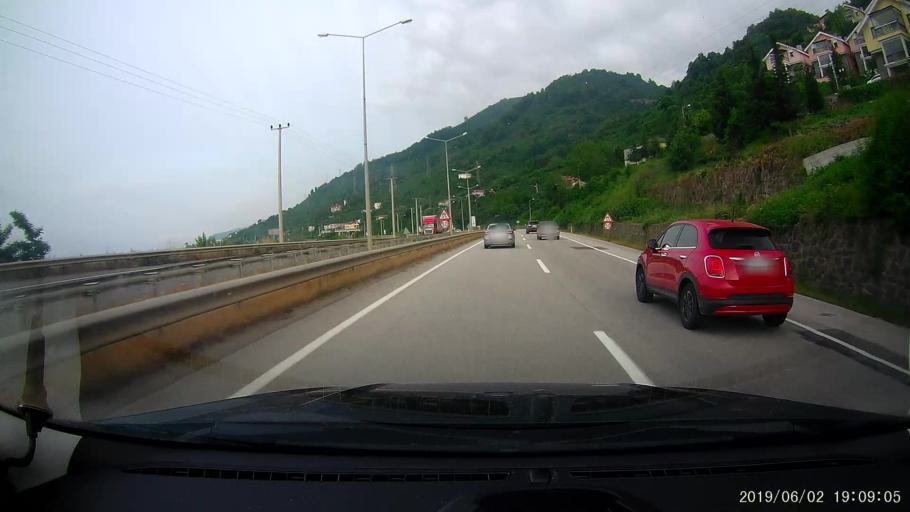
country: TR
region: Ordu
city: Gulyali
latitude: 40.9751
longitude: 38.0216
